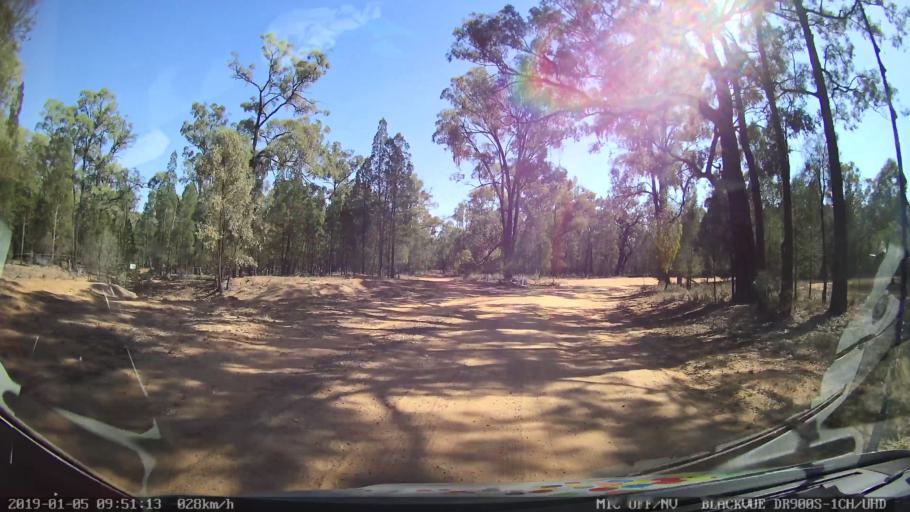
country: AU
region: New South Wales
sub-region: Gilgandra
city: Gilgandra
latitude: -31.6611
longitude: 148.7595
